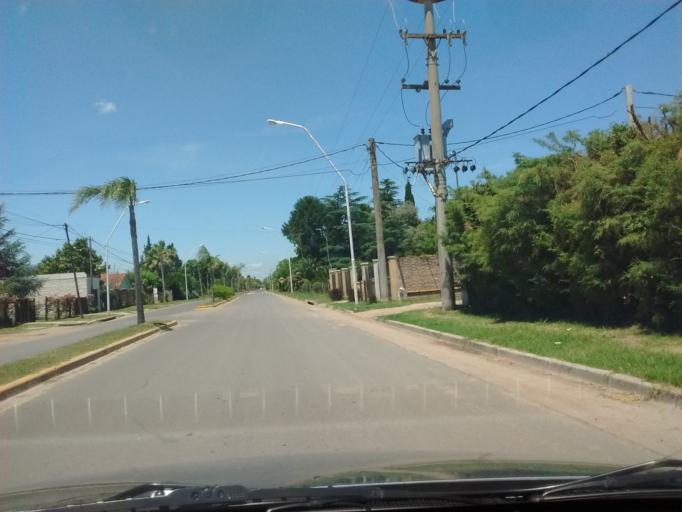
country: AR
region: Entre Rios
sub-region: Departamento de Gualeguay
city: Gualeguay
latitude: -33.1276
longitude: -59.3224
